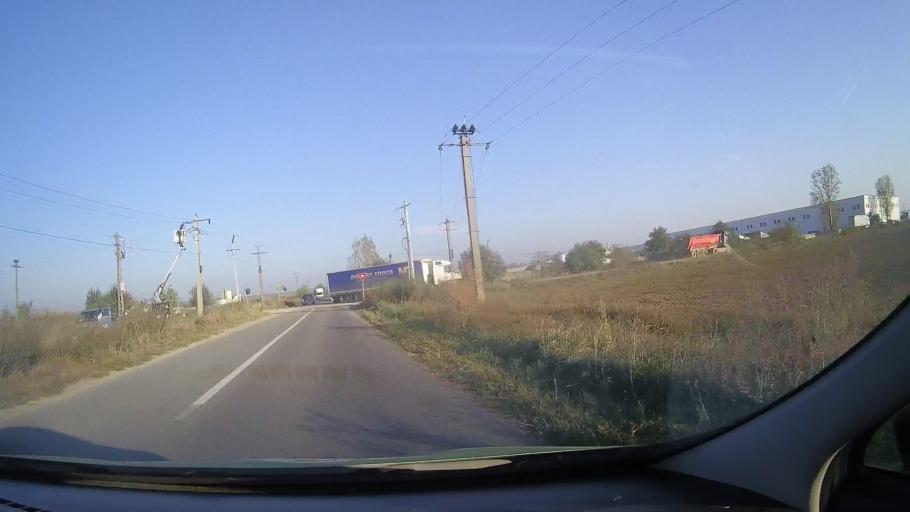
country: RO
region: Bihor
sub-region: Comuna Bors
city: Santion
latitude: 47.1141
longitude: 21.8463
